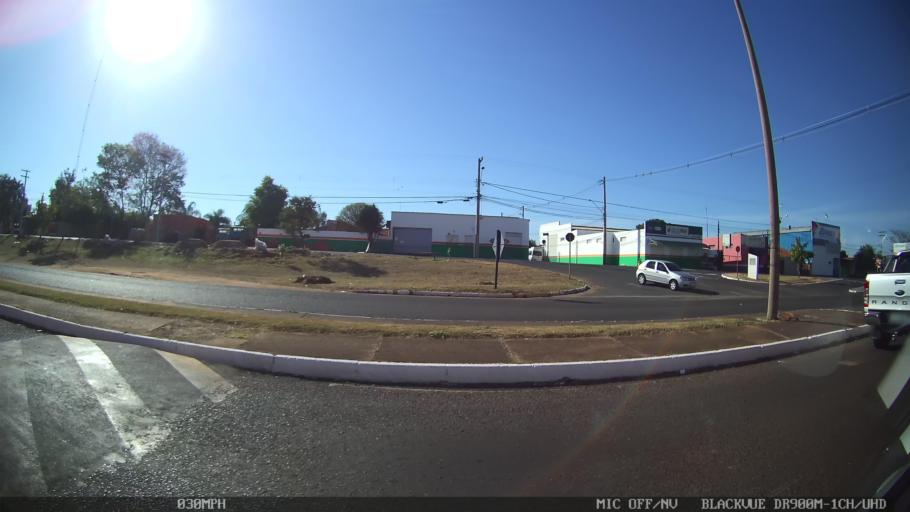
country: BR
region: Sao Paulo
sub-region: Olimpia
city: Olimpia
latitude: -20.7383
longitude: -48.8932
